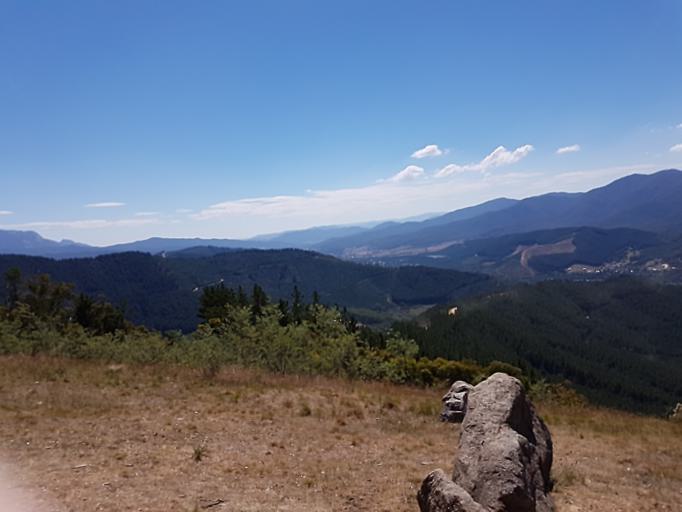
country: AU
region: Victoria
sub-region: Alpine
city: Mount Beauty
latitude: -36.7585
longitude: 146.9653
